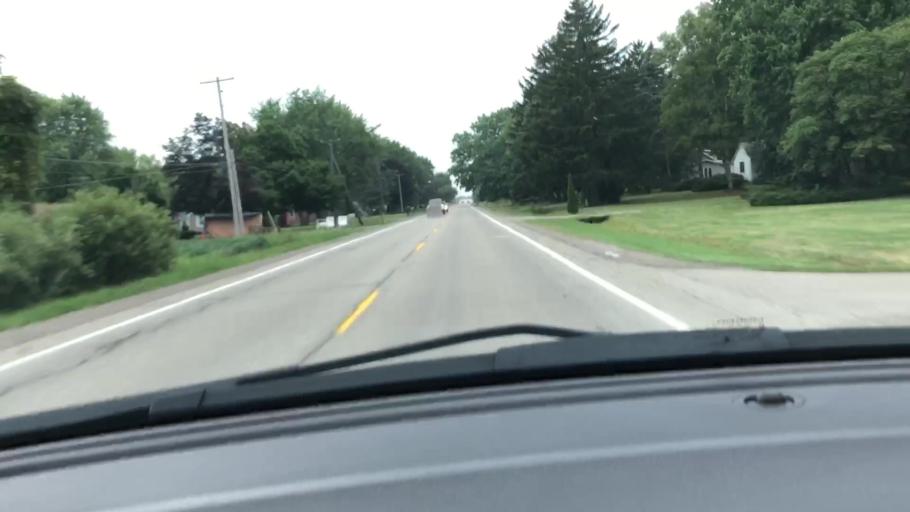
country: US
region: Michigan
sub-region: Bay County
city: Auburn
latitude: 43.6045
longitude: -84.1422
